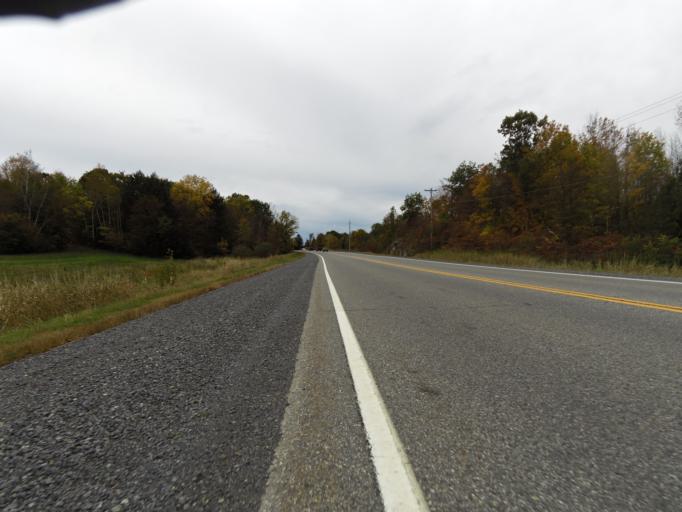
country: CA
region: Ontario
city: Gananoque
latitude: 44.4205
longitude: -76.3026
